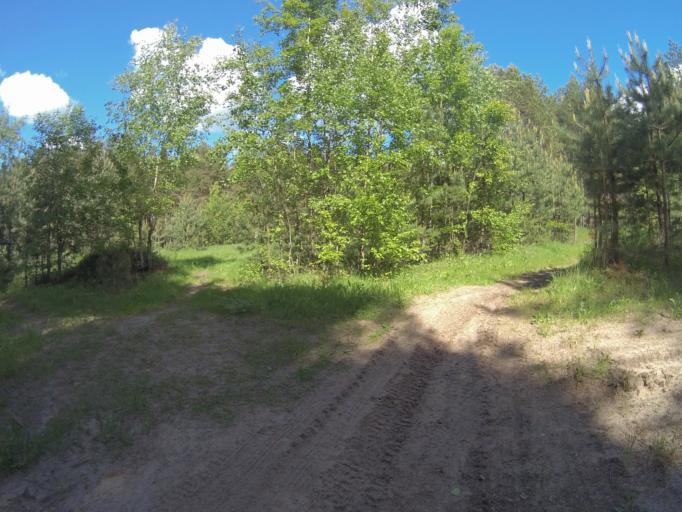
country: RU
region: Vladimir
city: Kommunar
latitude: 56.0691
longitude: 40.4381
